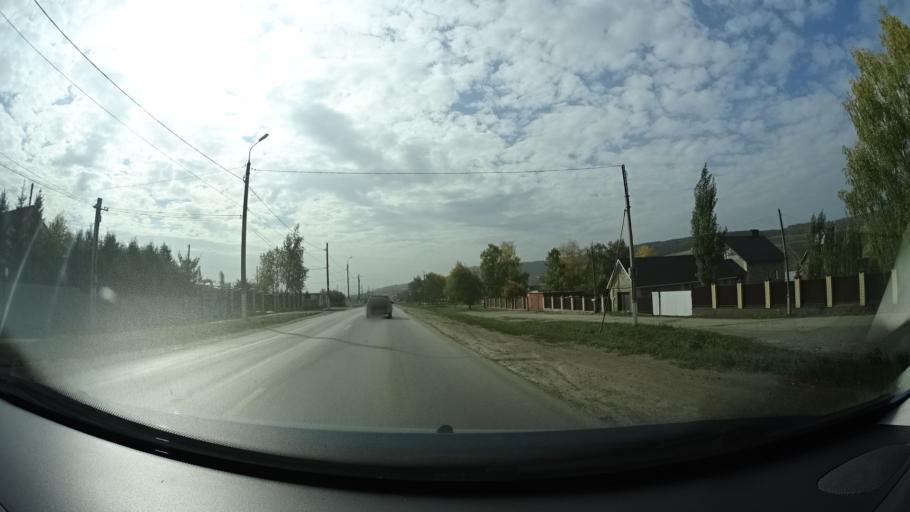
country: RU
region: Bashkortostan
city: Oktyabr'skiy
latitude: 54.5139
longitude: 53.5228
